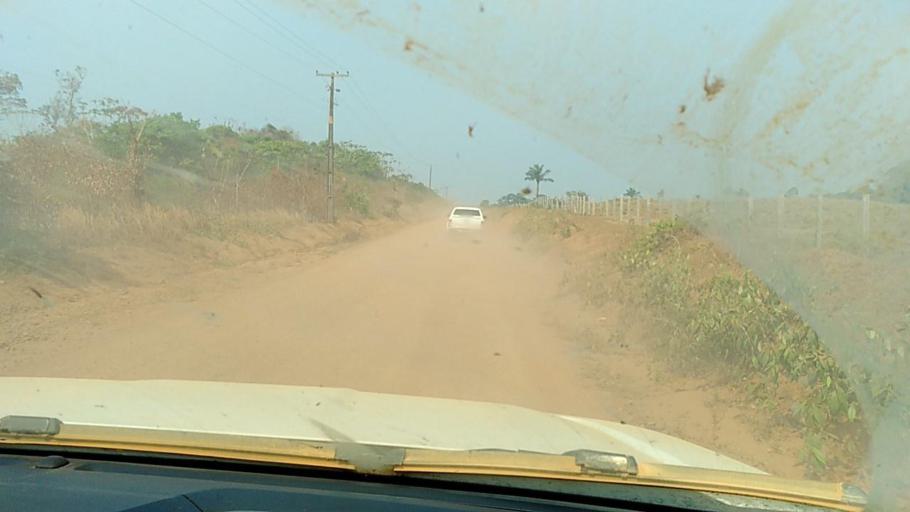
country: BR
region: Rondonia
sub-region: Porto Velho
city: Porto Velho
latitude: -8.8379
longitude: -64.1482
